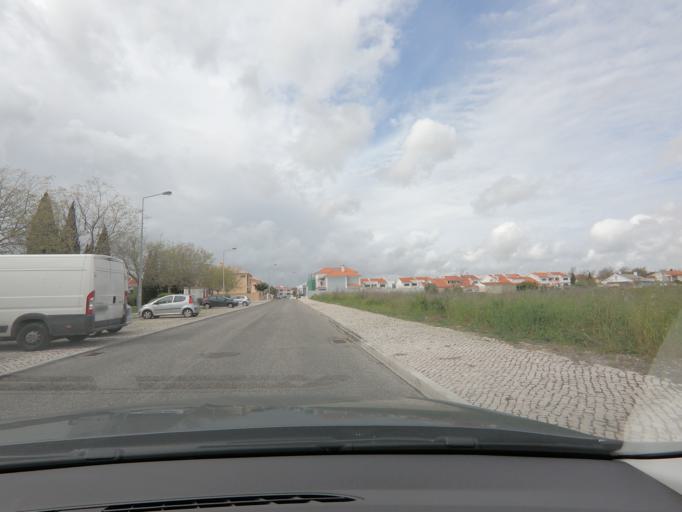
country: PT
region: Lisbon
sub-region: Cascais
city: Sao Domingos de Rana
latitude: 38.7282
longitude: -9.3295
